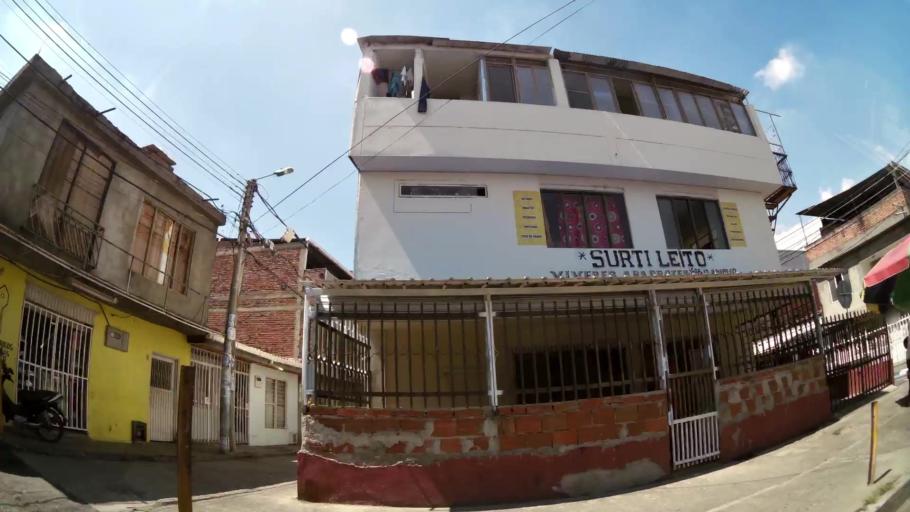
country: CO
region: Valle del Cauca
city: Cali
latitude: 3.4266
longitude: -76.5022
